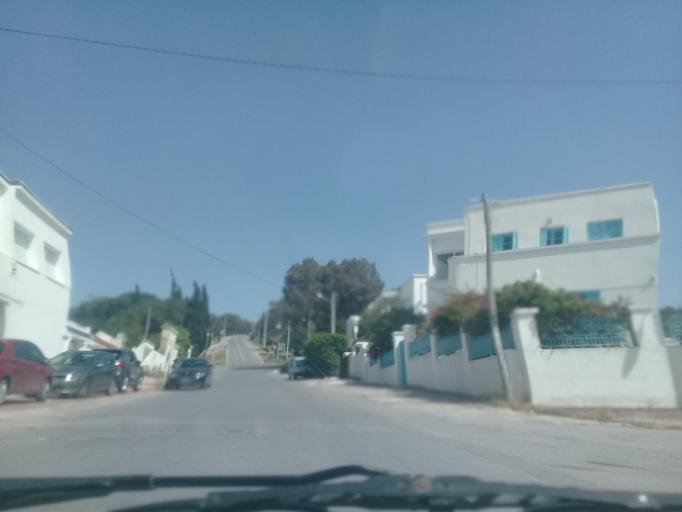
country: TN
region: Tunis
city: Sidi Bou Said
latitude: 36.8798
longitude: 10.3396
